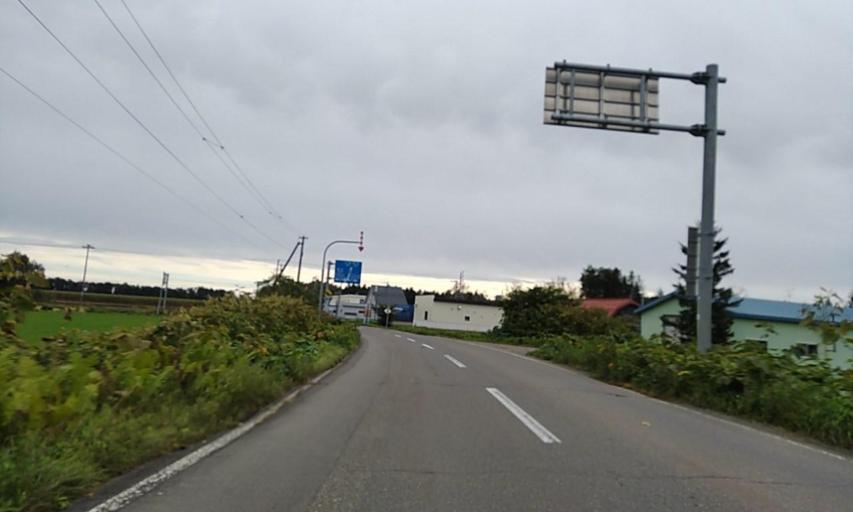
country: JP
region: Hokkaido
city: Obihiro
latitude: 42.6406
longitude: 143.0927
